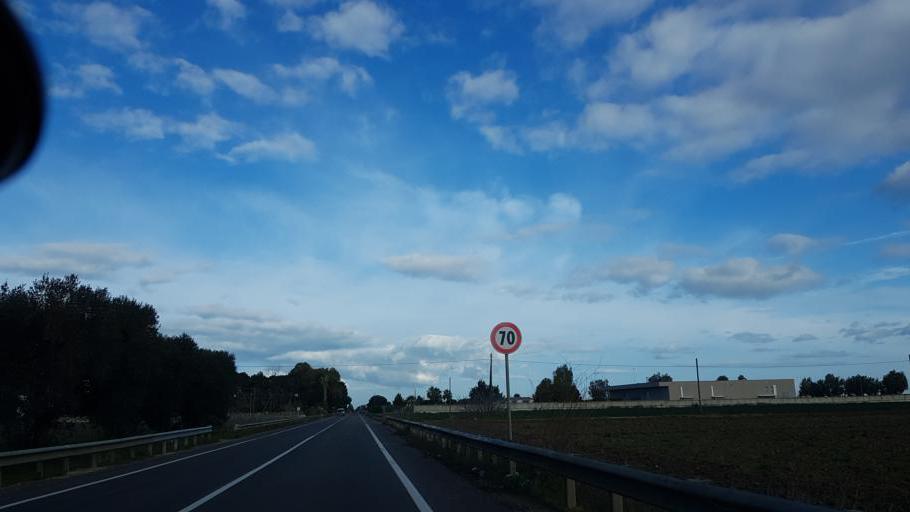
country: IT
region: Apulia
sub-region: Provincia di Brindisi
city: Tuturano
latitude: 40.5675
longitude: 17.9697
